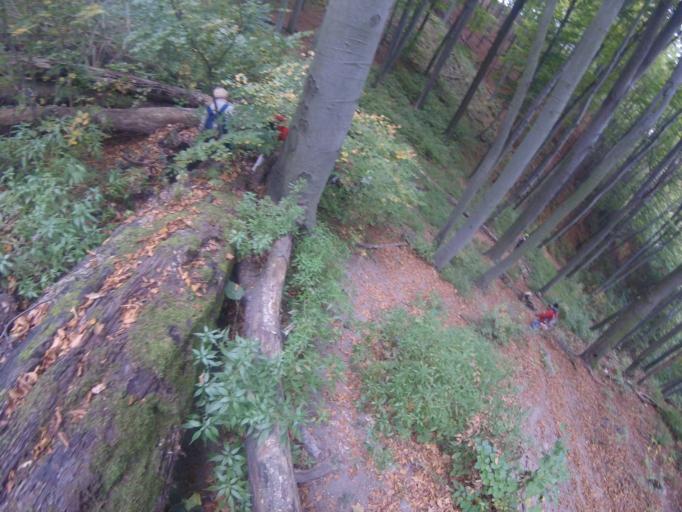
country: HU
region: Gyor-Moson-Sopron
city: Bakonyszentlaszlo
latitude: 47.2919
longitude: 17.7592
